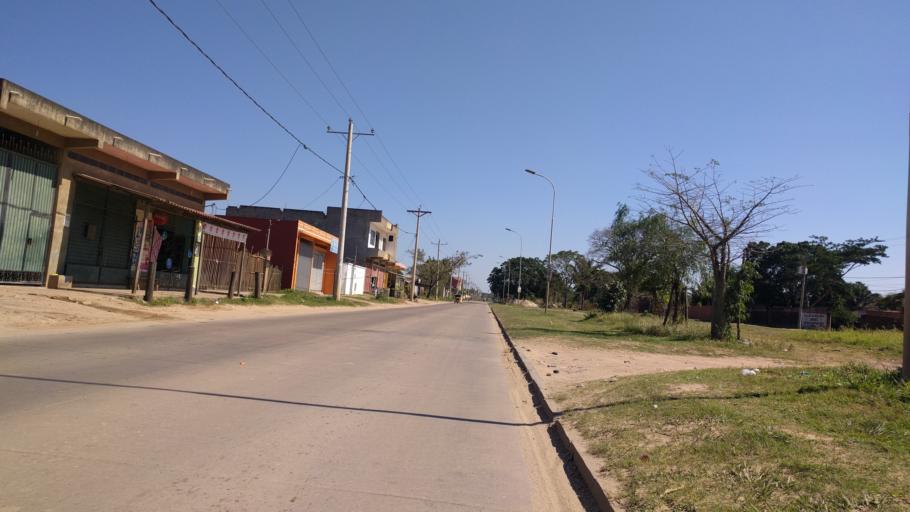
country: BO
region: Santa Cruz
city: Santa Cruz de la Sierra
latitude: -17.8488
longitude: -63.2048
